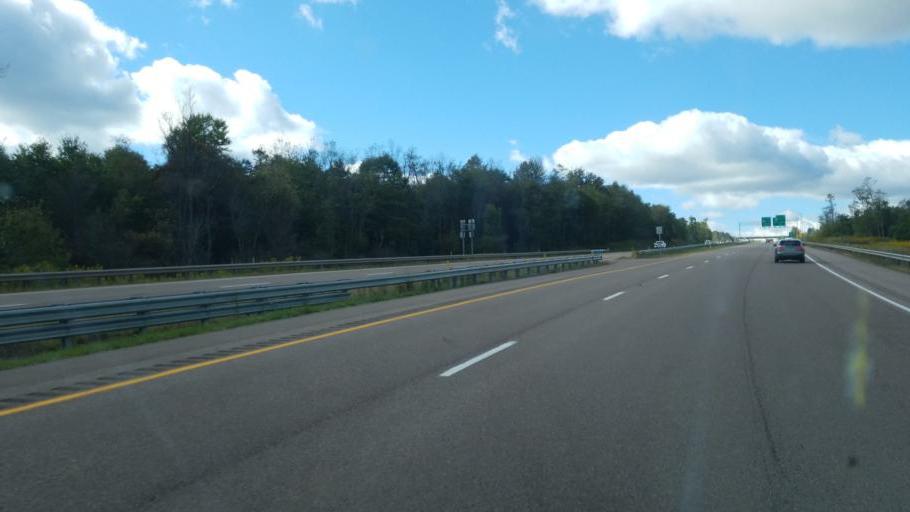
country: US
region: Pennsylvania
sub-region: Somerset County
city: Meyersdale
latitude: 39.6821
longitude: -79.2385
